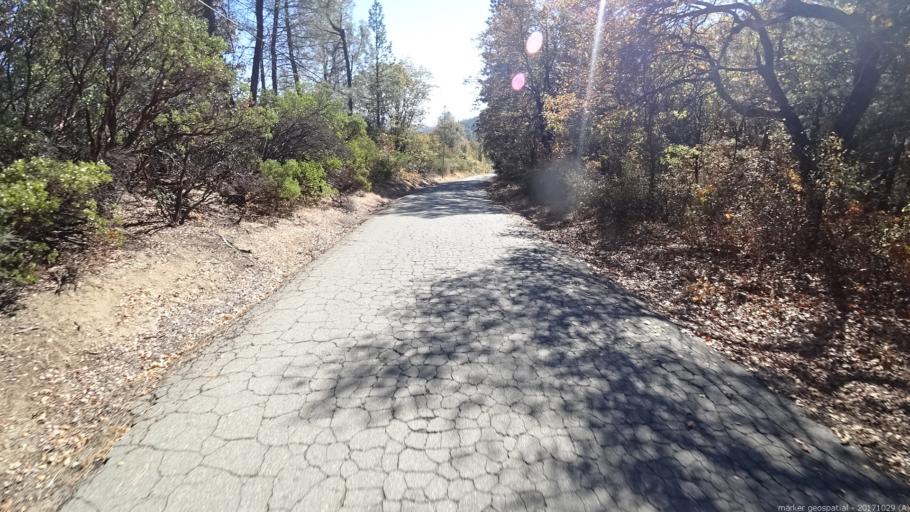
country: US
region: California
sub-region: Shasta County
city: Shasta
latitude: 40.4955
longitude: -122.6904
